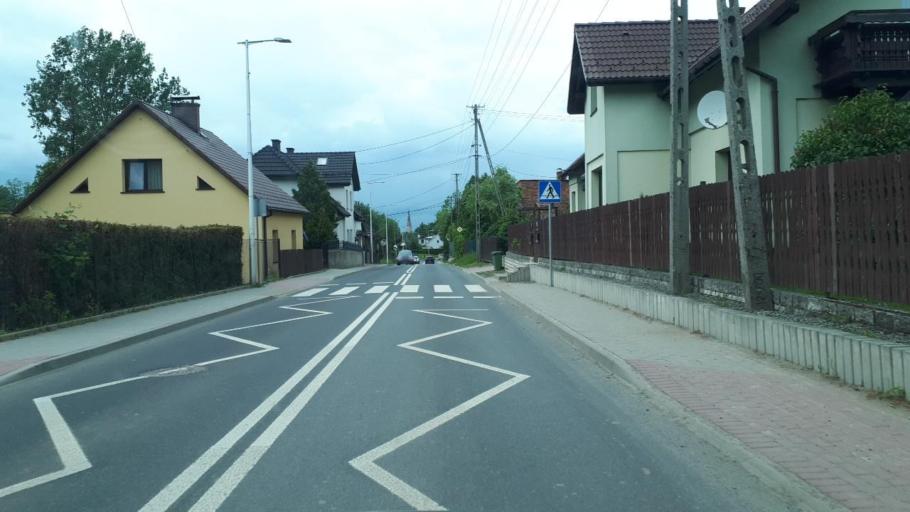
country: PL
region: Silesian Voivodeship
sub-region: Powiat bielski
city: Kozy
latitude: 49.8412
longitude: 19.1463
